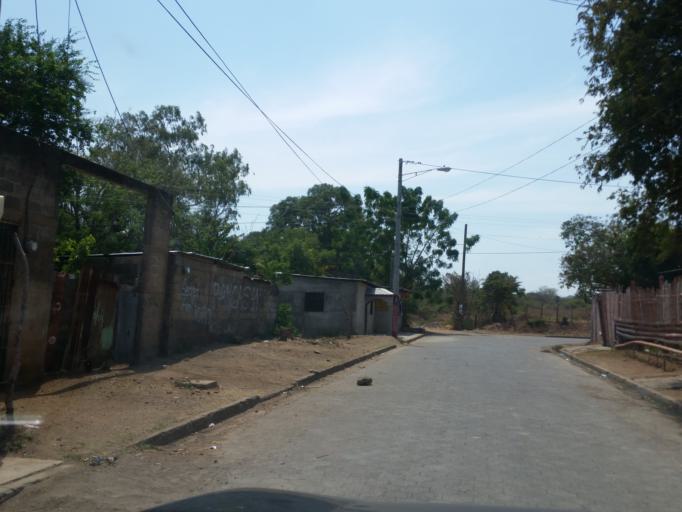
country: NI
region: Granada
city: Granada
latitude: 11.9440
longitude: -85.9653
